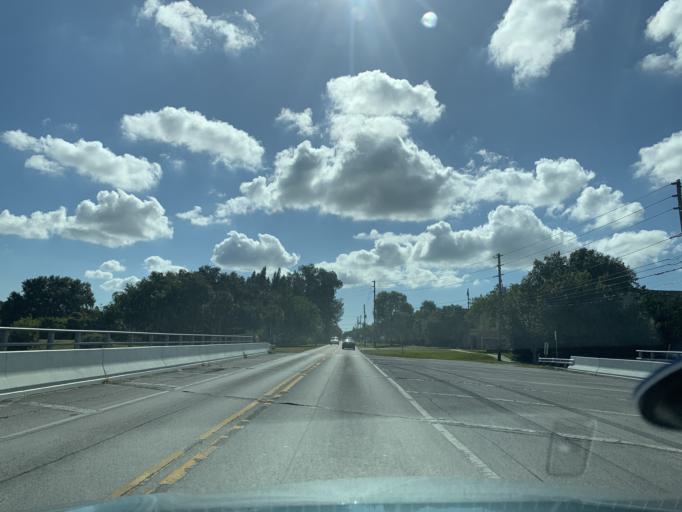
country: US
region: Florida
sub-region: Pinellas County
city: Kenneth City
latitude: 27.8121
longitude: -82.7369
